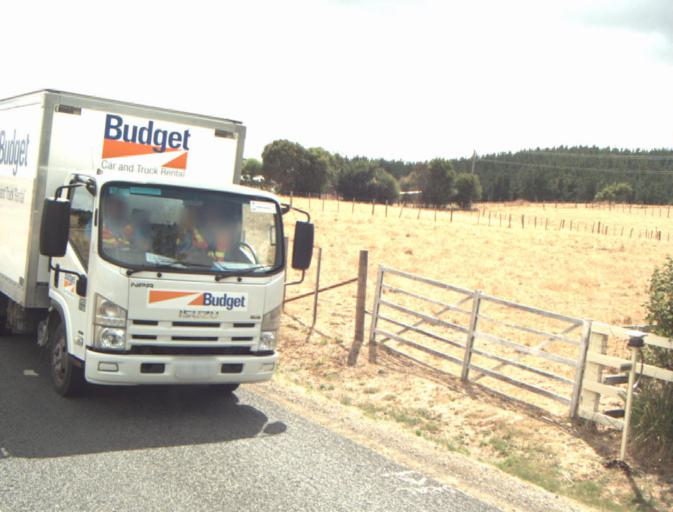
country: AU
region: Tasmania
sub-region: Launceston
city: Mayfield
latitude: -41.1896
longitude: 147.2215
